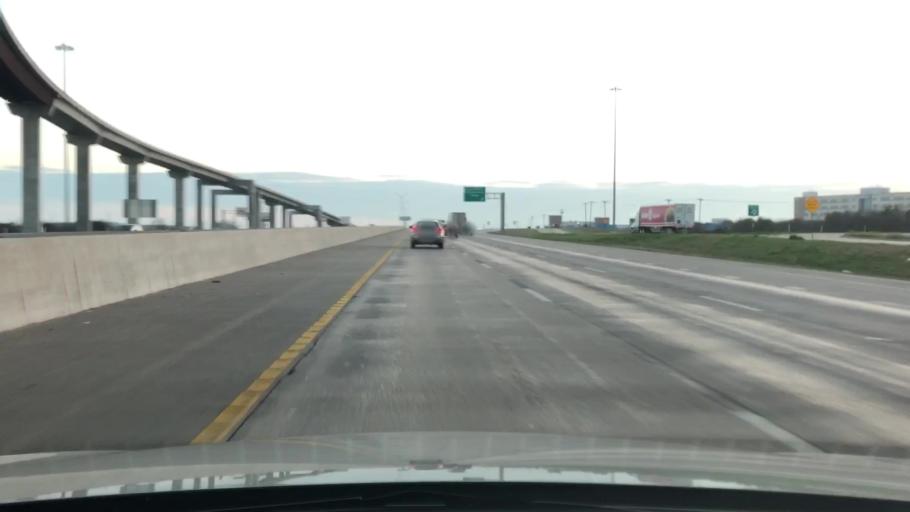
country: US
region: Texas
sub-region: McLennan County
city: Beverly Hills
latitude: 31.4927
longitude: -97.1515
